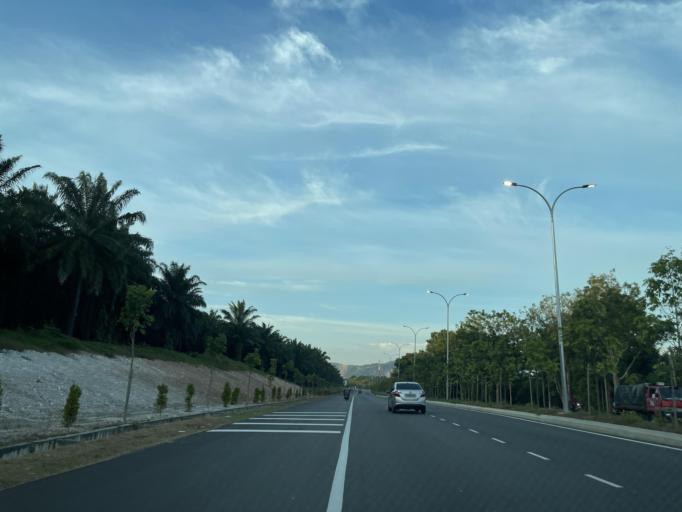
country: MY
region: Melaka
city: Kampung Ayer Keroh
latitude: 2.3206
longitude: 102.2490
